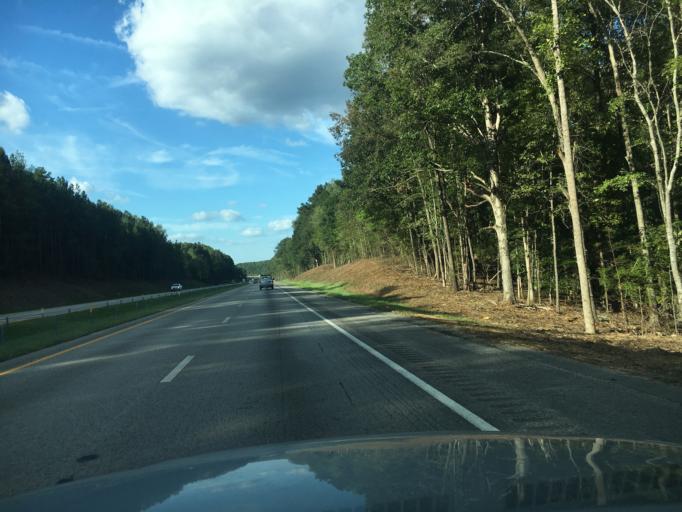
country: US
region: South Carolina
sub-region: Laurens County
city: Clinton
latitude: 34.5872
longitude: -81.8925
